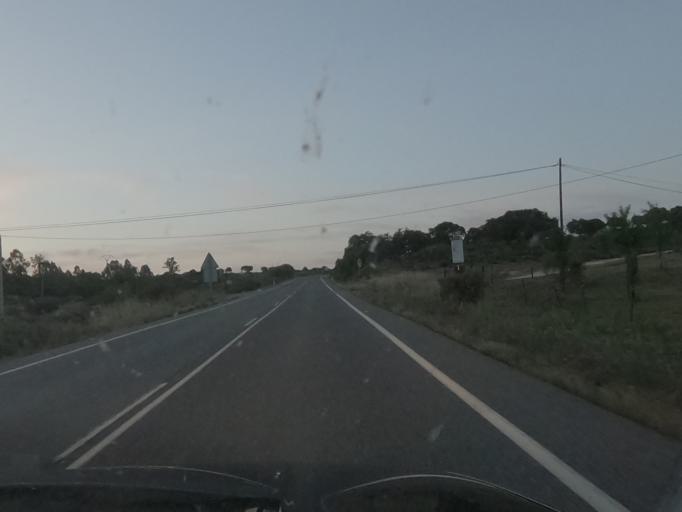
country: ES
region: Extremadura
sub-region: Provincia de Caceres
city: Alcantara
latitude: 39.7484
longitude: -6.9029
